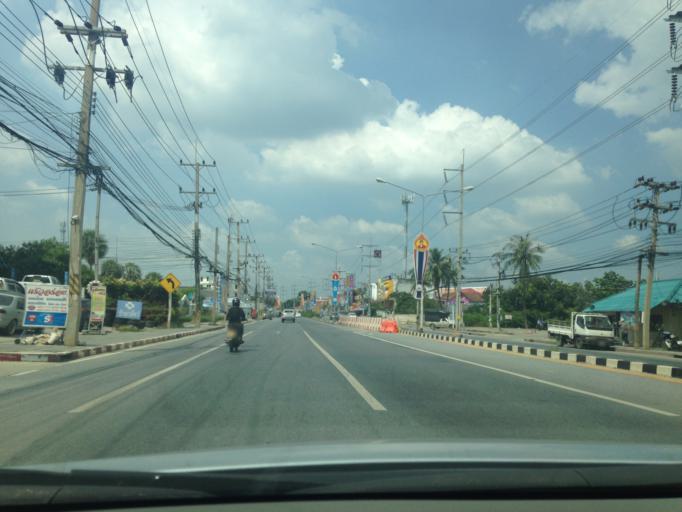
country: TH
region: Pathum Thani
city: Sam Khok
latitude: 14.0644
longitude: 100.5235
